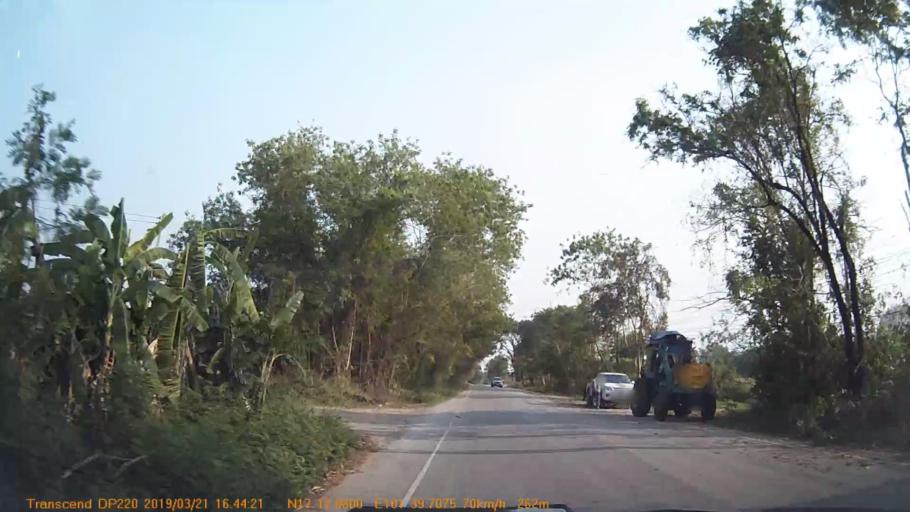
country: TH
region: Loei
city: Phu Luang
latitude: 17.2011
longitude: 101.6619
